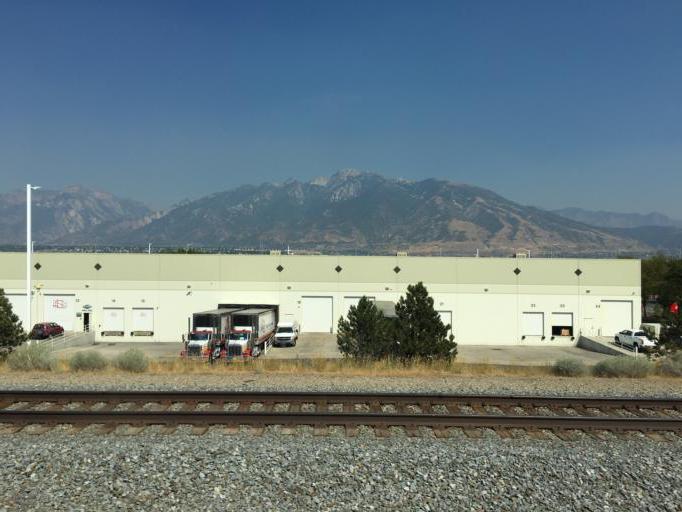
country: US
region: Utah
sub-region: Salt Lake County
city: Riverton
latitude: 40.5250
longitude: -111.9047
